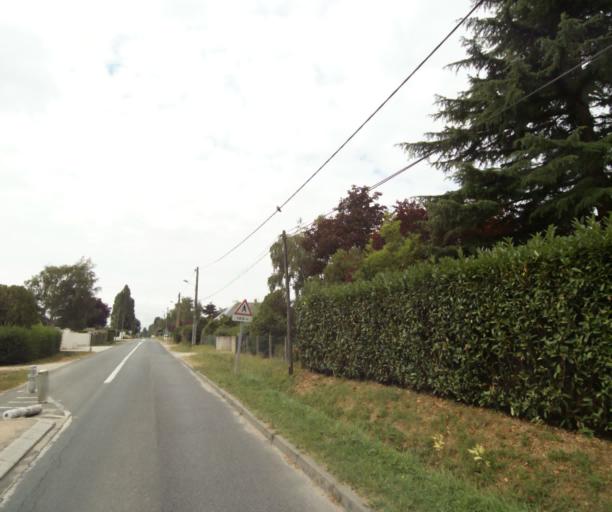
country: FR
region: Centre
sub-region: Departement du Loiret
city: Boigny-sur-Bionne
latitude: 47.9218
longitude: 2.0439
